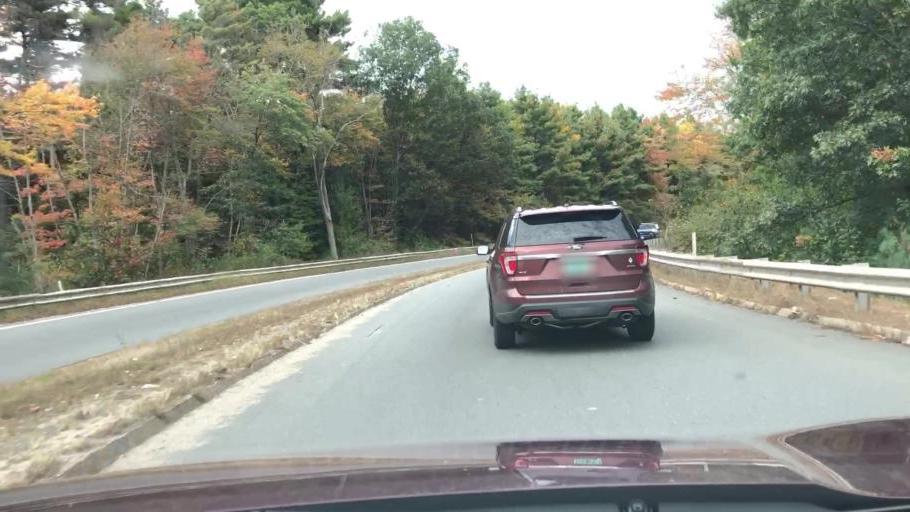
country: US
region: Massachusetts
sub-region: Essex County
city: Lawrence
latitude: 42.6644
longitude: -71.1971
